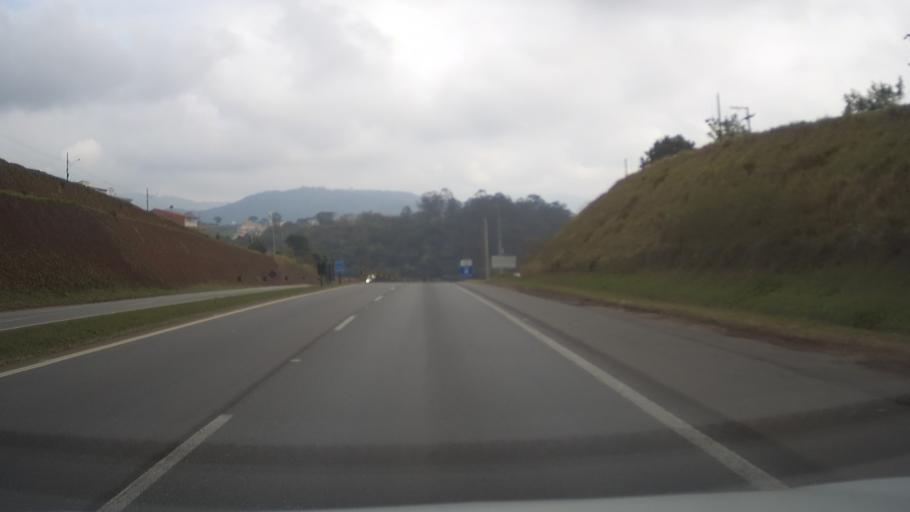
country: BR
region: Minas Gerais
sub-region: Extrema
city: Extrema
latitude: -22.8536
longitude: -46.3372
